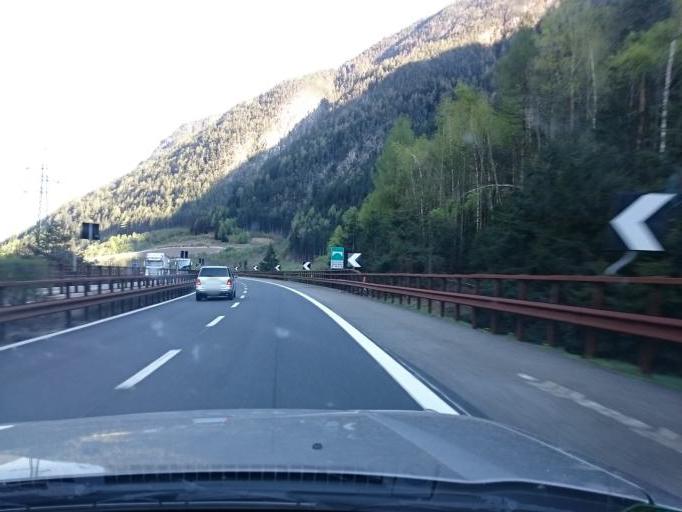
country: IT
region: Trentino-Alto Adige
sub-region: Bolzano
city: Fortezza
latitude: 46.8163
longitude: 11.5390
